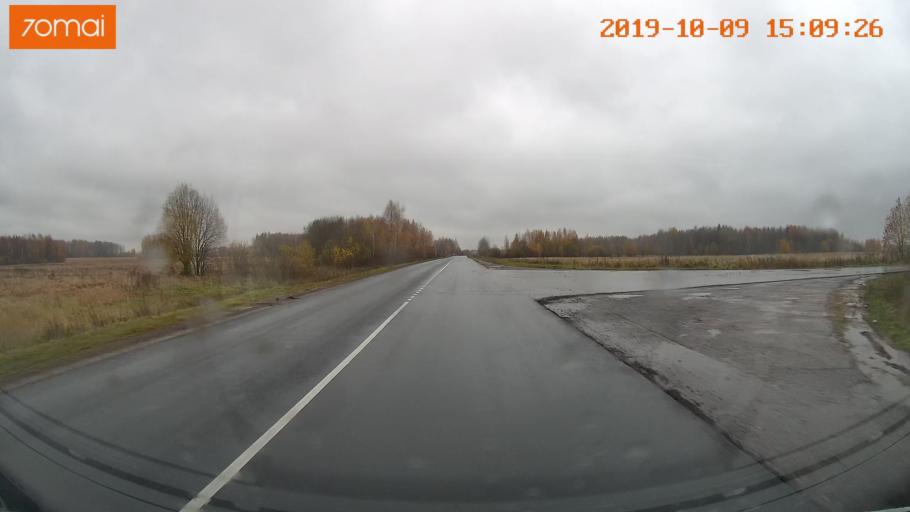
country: RU
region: Kostroma
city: Susanino
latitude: 58.1915
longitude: 41.6502
